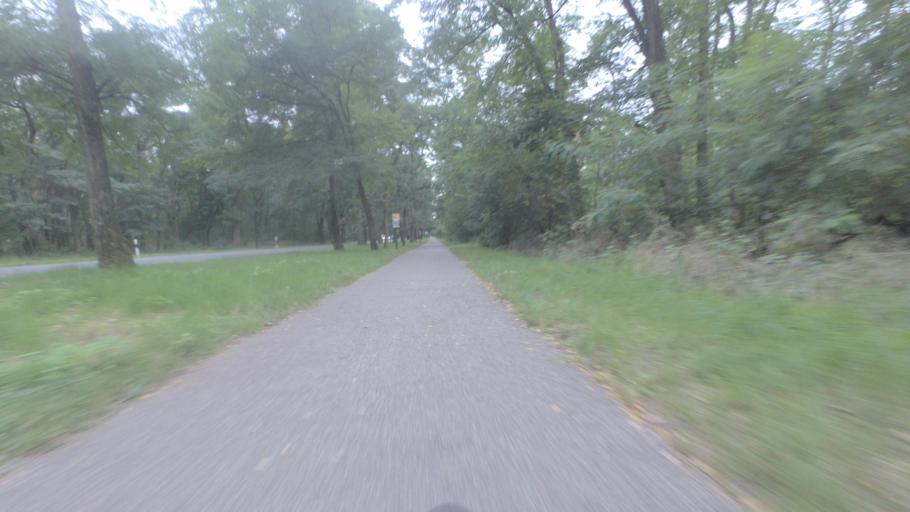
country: DE
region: Berlin
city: Mahlsdorf
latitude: 52.4900
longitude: 13.6349
